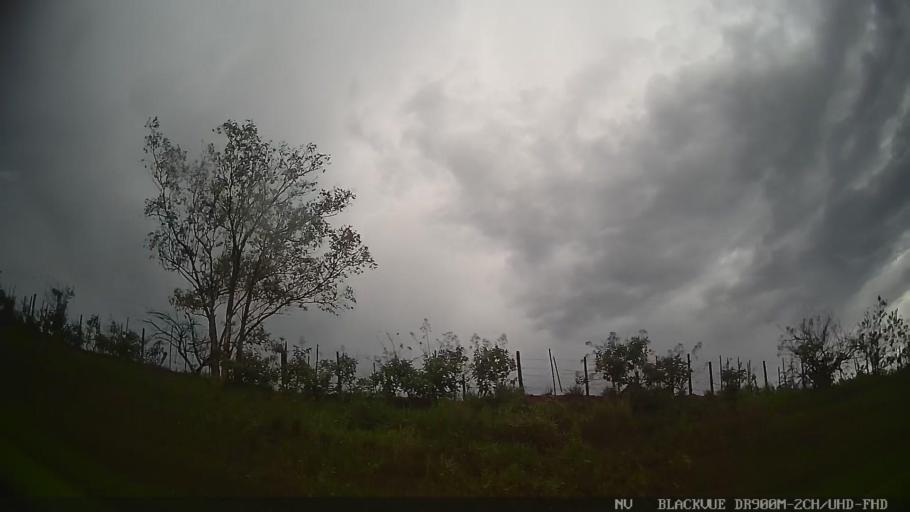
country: BR
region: Sao Paulo
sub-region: Pedreira
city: Pedreira
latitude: -22.7254
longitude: -46.9340
